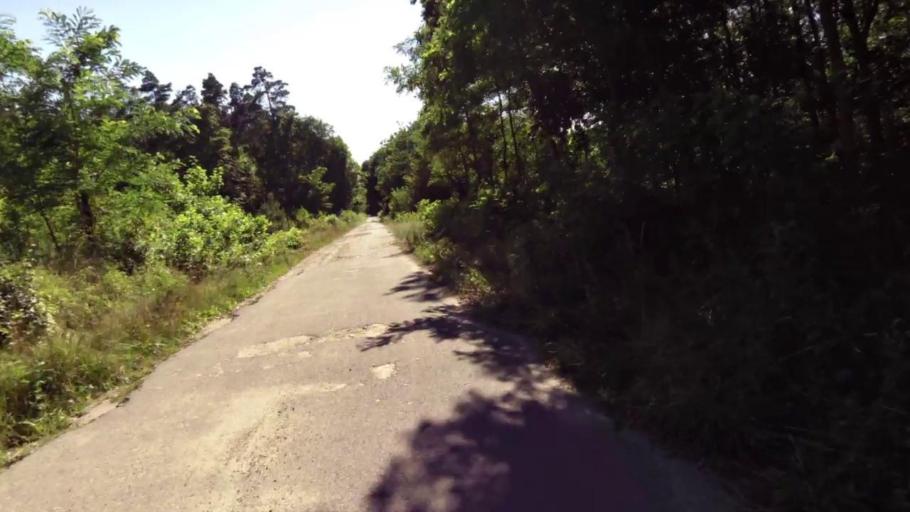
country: PL
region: West Pomeranian Voivodeship
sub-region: Powiat szczecinecki
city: Borne Sulinowo
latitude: 53.5913
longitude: 16.5785
